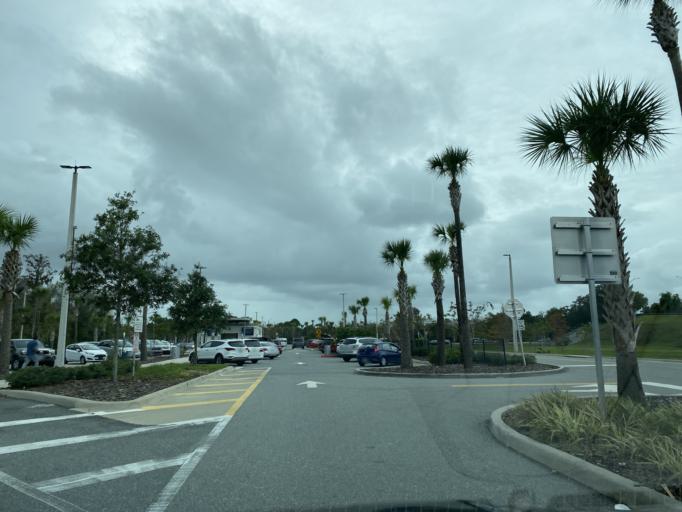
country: US
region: Florida
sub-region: Orange County
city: Belle Isle
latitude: 28.4412
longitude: -81.3090
